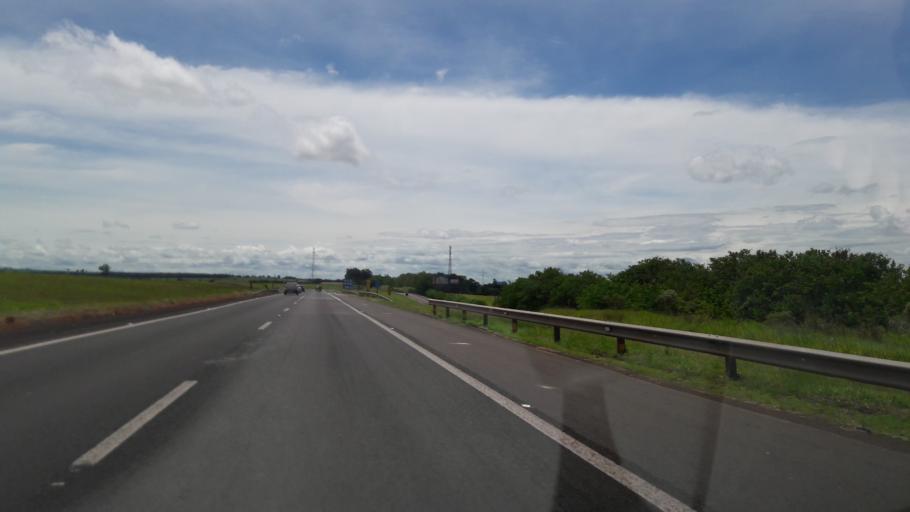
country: BR
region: Sao Paulo
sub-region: Avare
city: Avare
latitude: -22.9568
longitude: -48.8498
